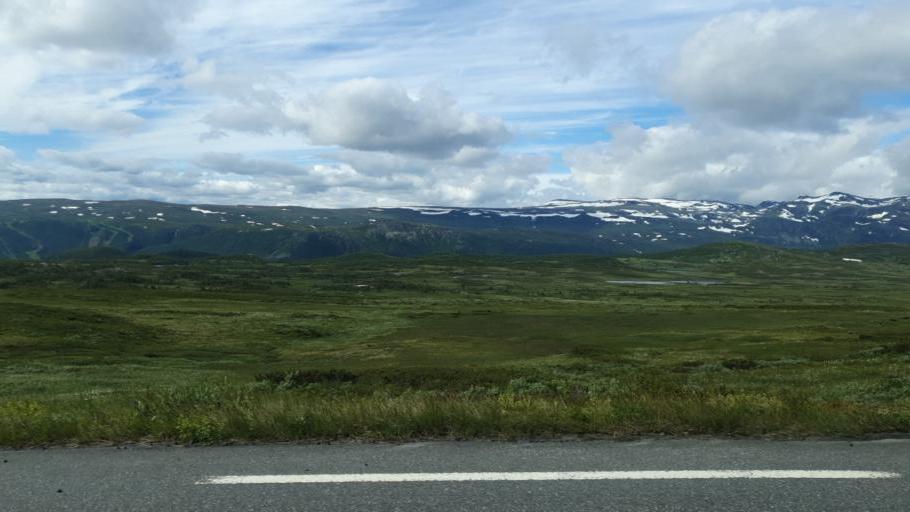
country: NO
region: Oppland
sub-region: Vestre Slidre
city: Slidre
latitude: 61.2757
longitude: 8.8559
